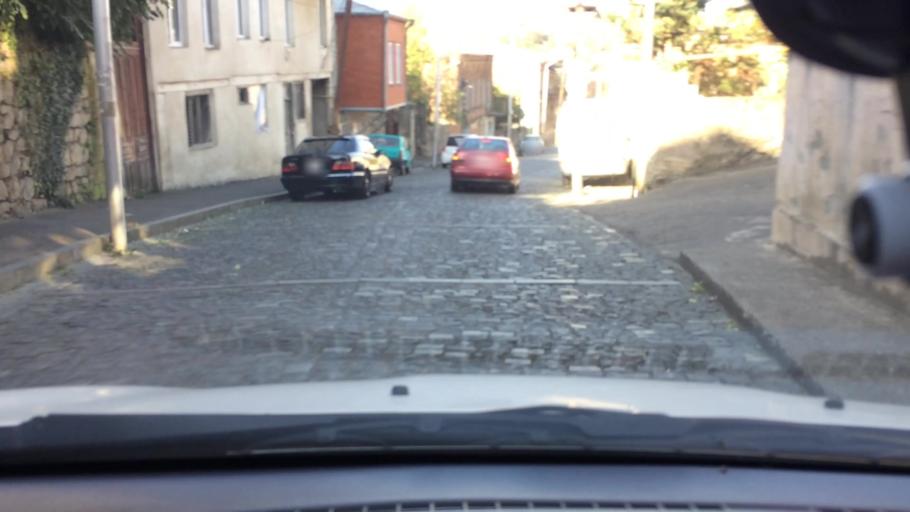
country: GE
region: Imereti
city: Kutaisi
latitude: 42.2726
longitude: 42.7108
